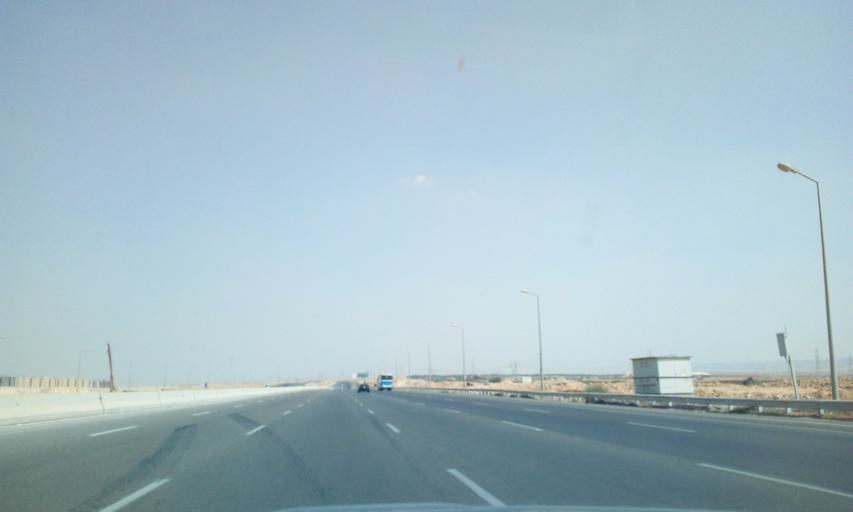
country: EG
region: Muhafazat al Qahirah
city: Halwan
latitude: 29.9149
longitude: 31.6330
